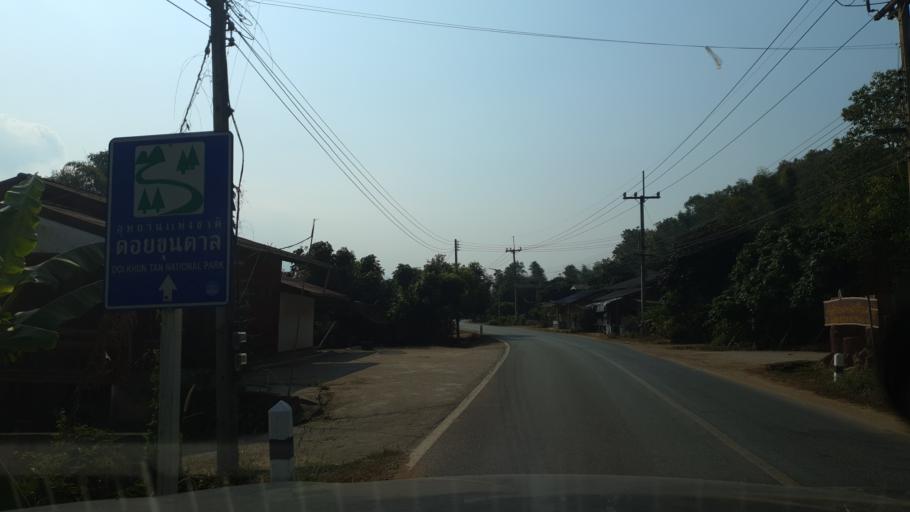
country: TH
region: Lamphun
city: Ban Thi
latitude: 18.5688
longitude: 99.2565
